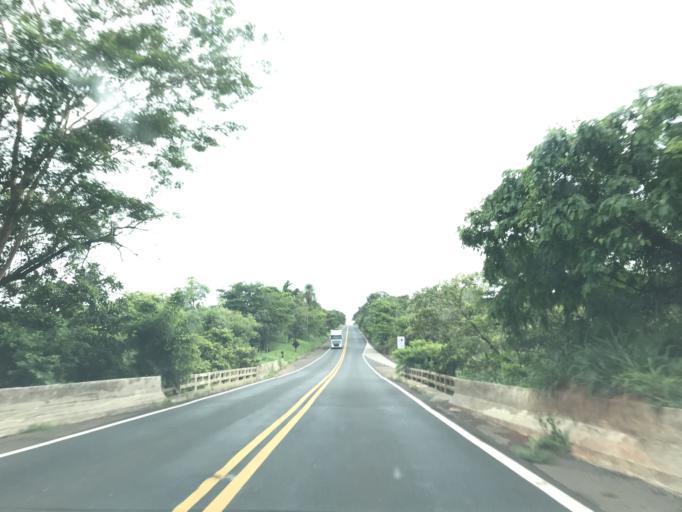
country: BR
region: Sao Paulo
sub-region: Penapolis
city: Penapolis
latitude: -21.4592
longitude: -50.1722
